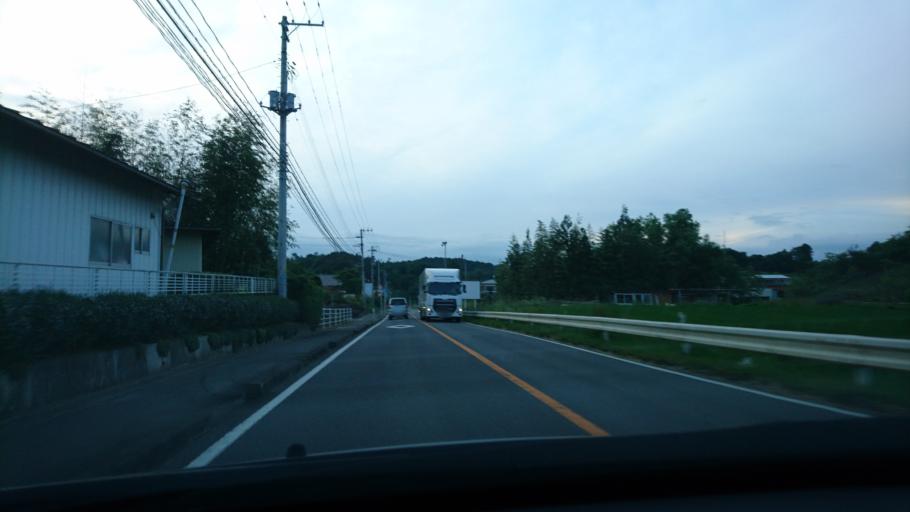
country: JP
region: Miyagi
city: Furukawa
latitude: 38.7561
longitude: 141.0063
